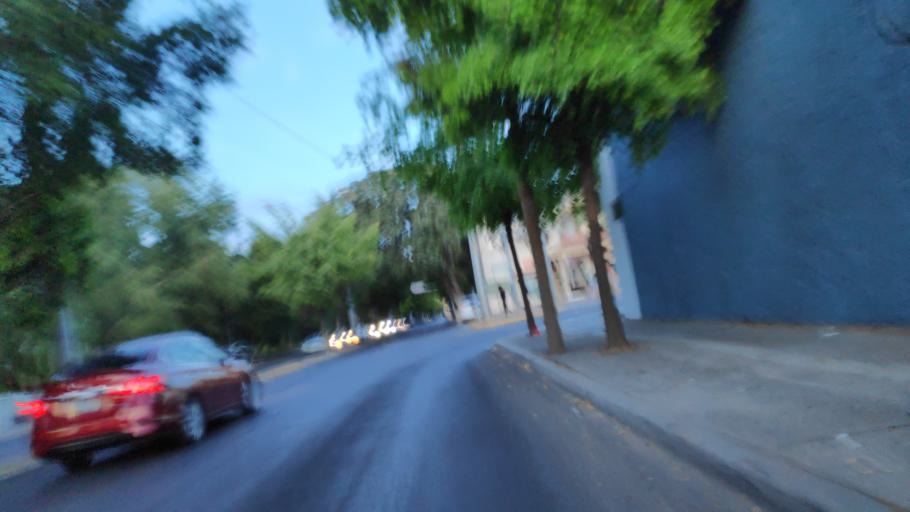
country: MX
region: Sinaloa
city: Culiacan
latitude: 24.8112
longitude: -107.4018
